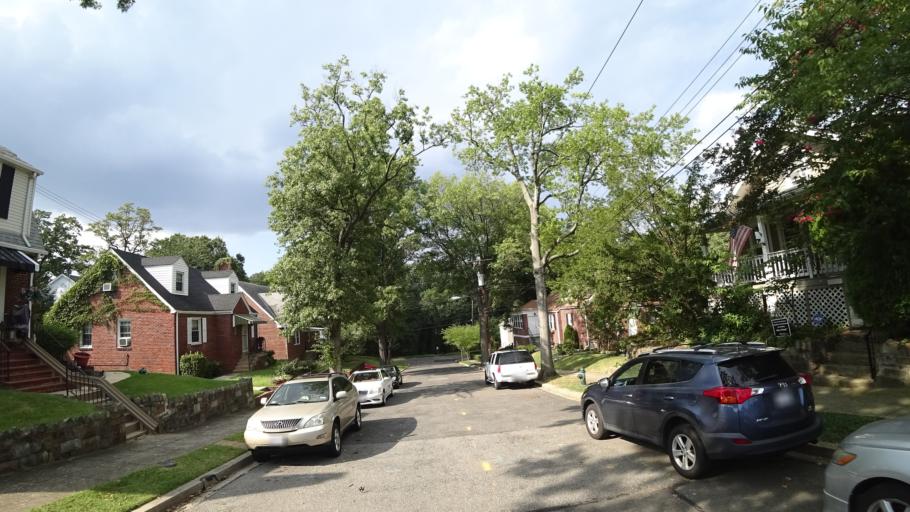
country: US
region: Maryland
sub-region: Prince George's County
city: Silver Hill
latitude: 38.8650
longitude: -76.9623
